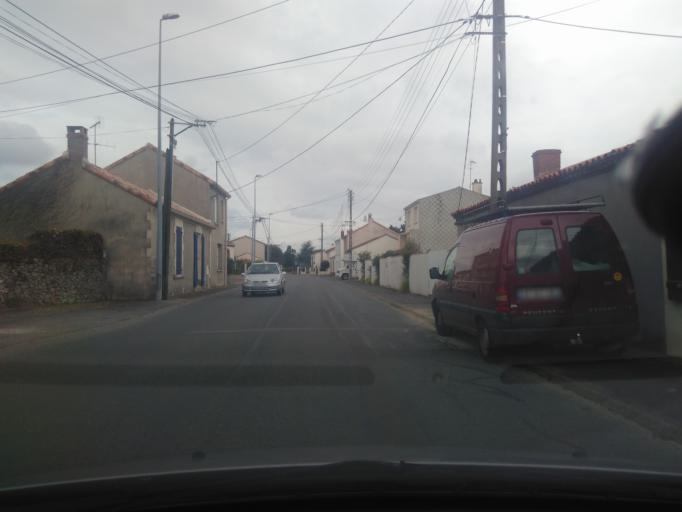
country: FR
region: Pays de la Loire
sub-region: Departement de la Vendee
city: La Roche-sur-Yon
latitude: 46.6638
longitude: -1.4081
